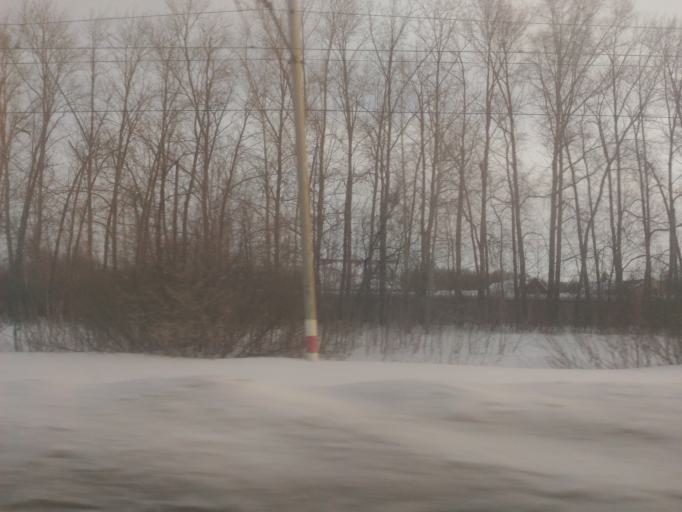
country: RU
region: Ulyanovsk
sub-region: Ulyanovskiy Rayon
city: Ulyanovsk
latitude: 54.3613
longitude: 48.3419
